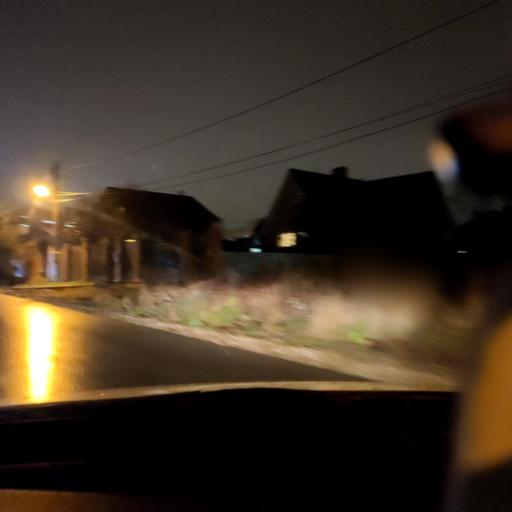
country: RU
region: Tatarstan
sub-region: Gorod Kazan'
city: Kazan
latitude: 55.7831
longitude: 49.2435
